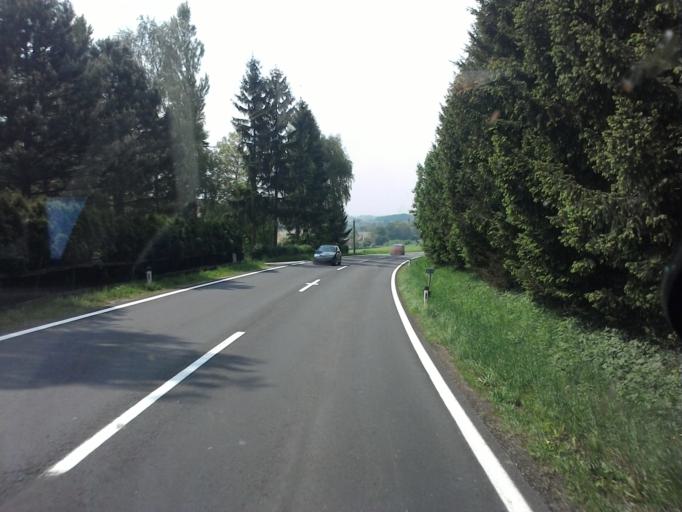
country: AT
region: Upper Austria
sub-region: Politischer Bezirk Kirchdorf an der Krems
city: Kremsmunster
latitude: 48.0639
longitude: 14.0984
